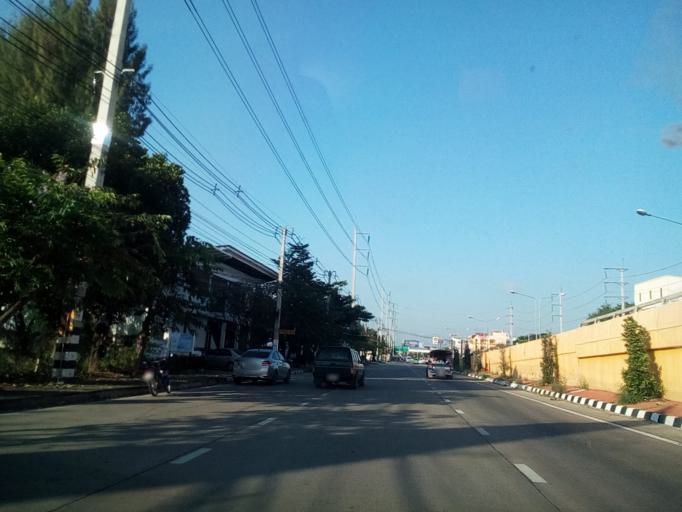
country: TH
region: Chiang Mai
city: Saraphi
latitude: 18.7630
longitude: 99.0279
